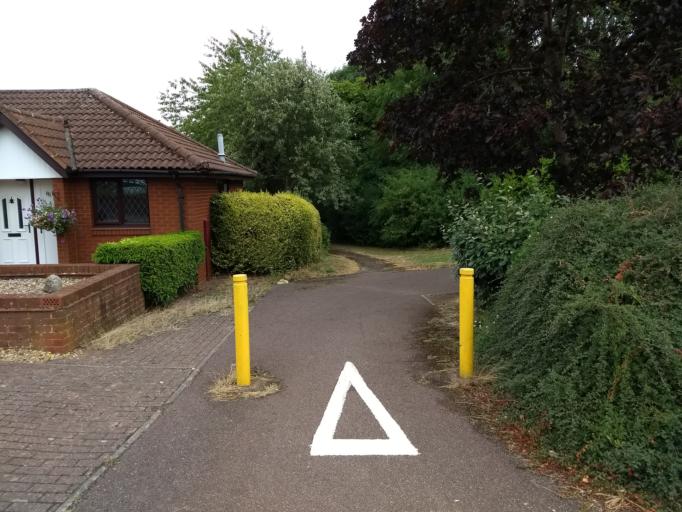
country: GB
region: England
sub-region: Milton Keynes
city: Bradwell
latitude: 52.0581
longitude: -0.7948
